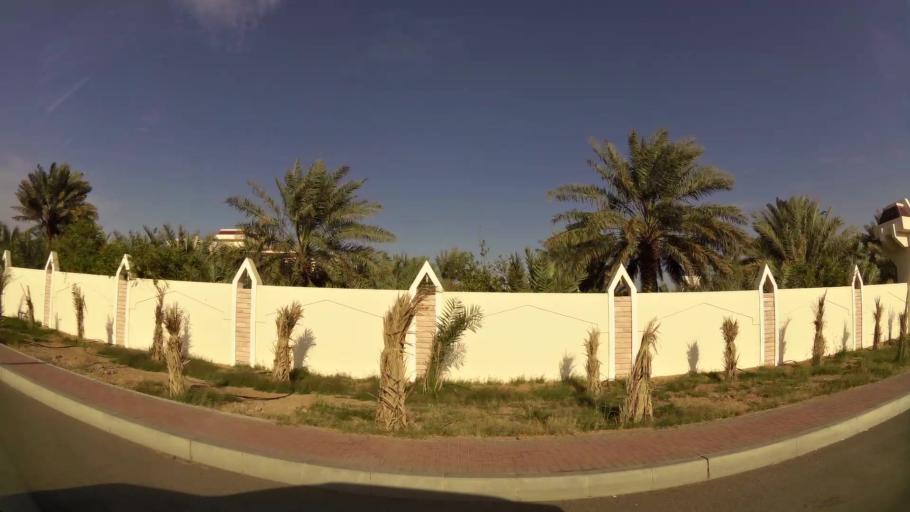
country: AE
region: Abu Dhabi
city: Al Ain
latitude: 24.0767
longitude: 55.8358
